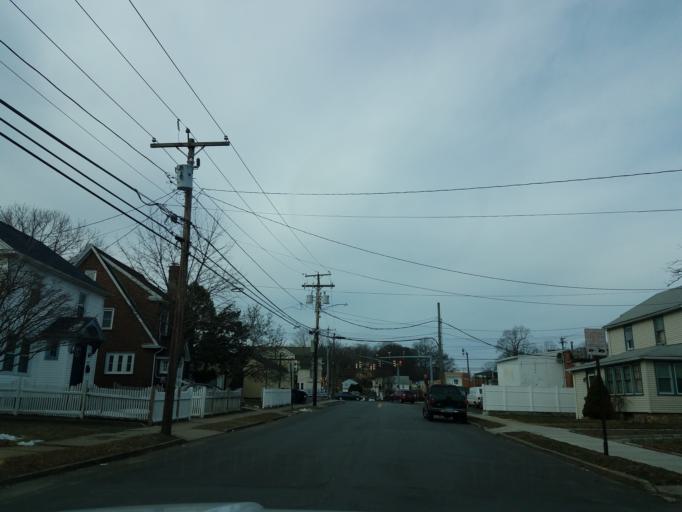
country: US
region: Connecticut
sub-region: Fairfield County
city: Trumbull
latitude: 41.2164
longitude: -73.2122
